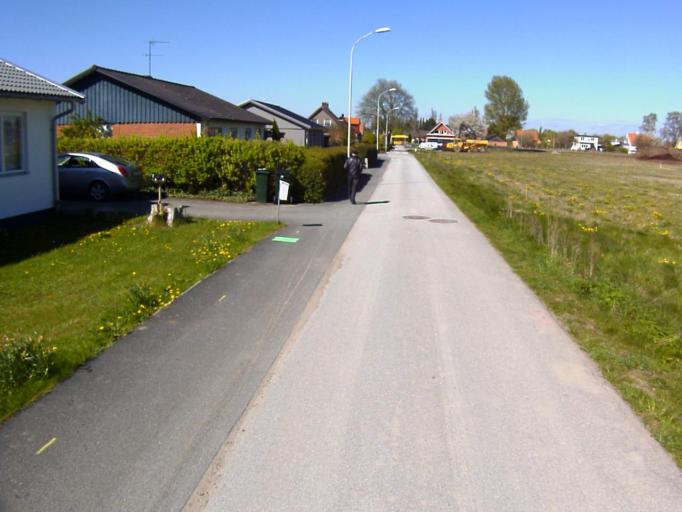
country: SE
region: Skane
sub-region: Kristianstads Kommun
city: Kristianstad
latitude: 56.0269
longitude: 14.1974
